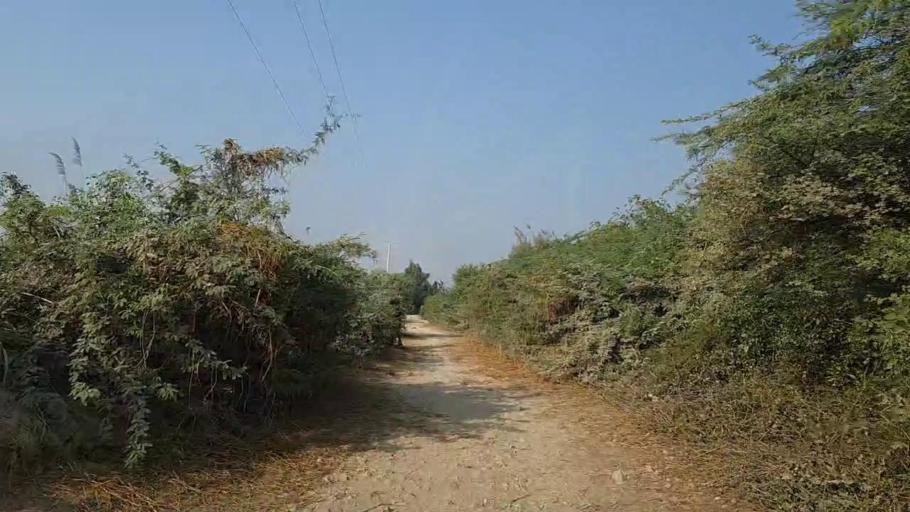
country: PK
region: Sindh
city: Mirpur Sakro
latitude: 24.6260
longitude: 67.7454
